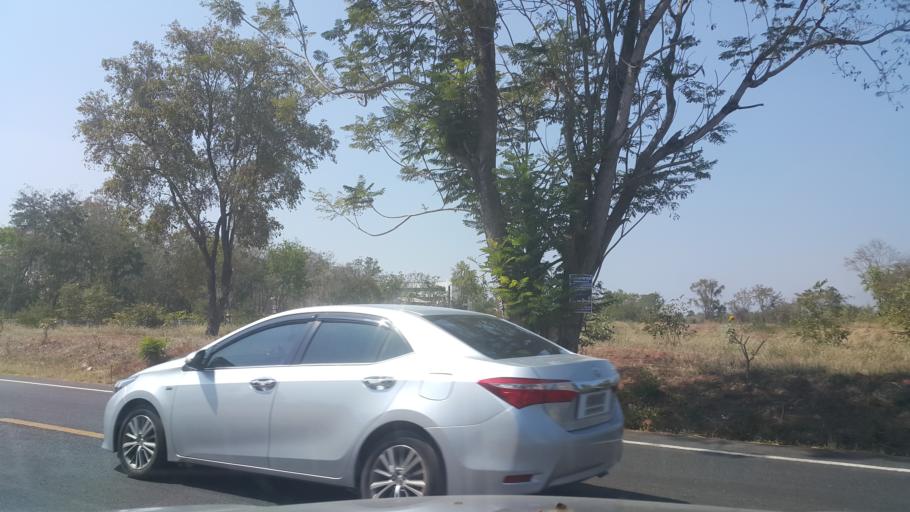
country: TH
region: Nakhon Ratchasima
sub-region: Amphoe Kaeng Sanam Nang
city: Kaeng Sanam Nang
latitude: 15.6869
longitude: 102.3294
